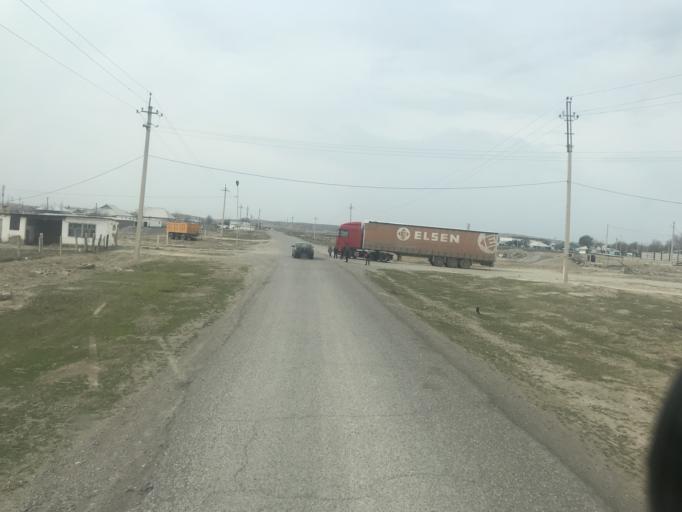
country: KZ
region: Ongtustik Qazaqstan
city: Shardara
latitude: 41.2617
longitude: 67.9422
